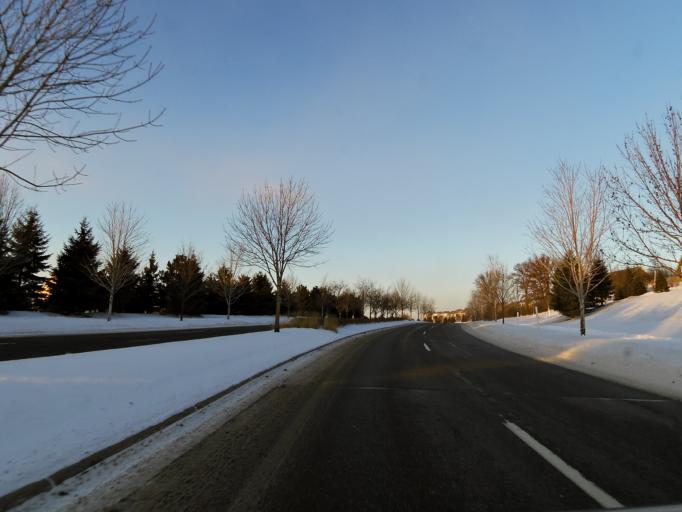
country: US
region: Minnesota
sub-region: Washington County
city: Lake Elmo
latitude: 44.9299
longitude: -92.8841
